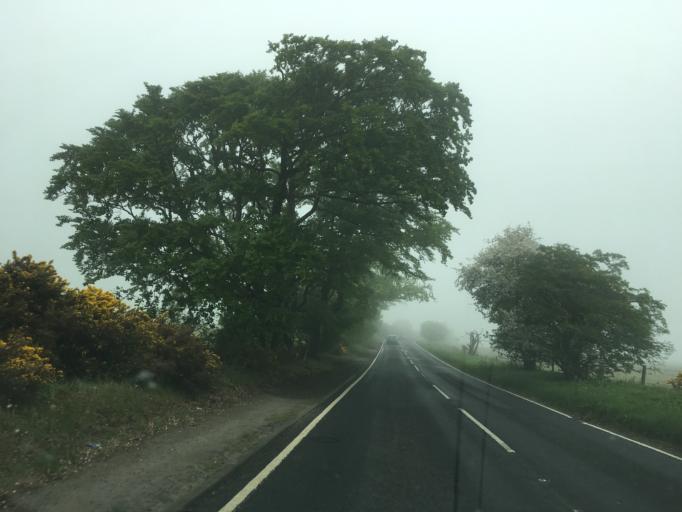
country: GB
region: Scotland
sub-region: Midlothian
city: Penicuik
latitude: 55.8217
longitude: -3.2023
